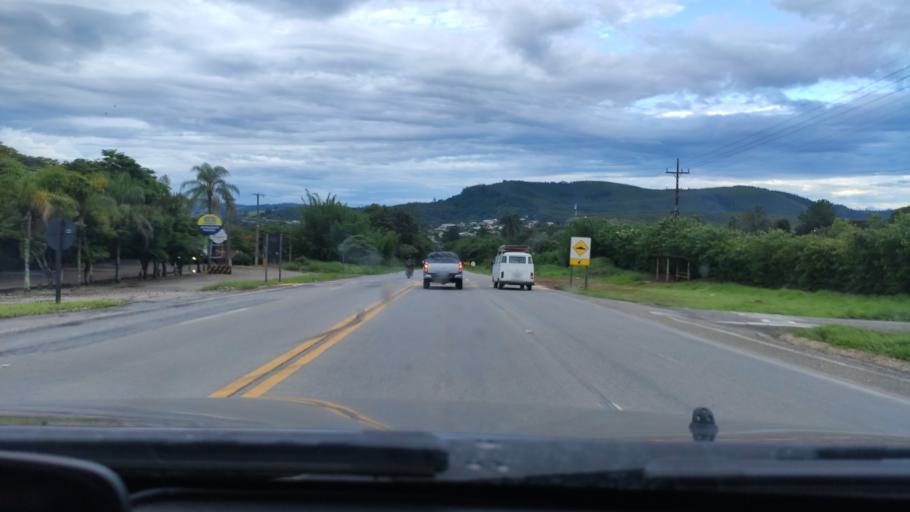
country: BR
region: Sao Paulo
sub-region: Braganca Paulista
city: Braganca Paulista
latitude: -22.8805
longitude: -46.5364
